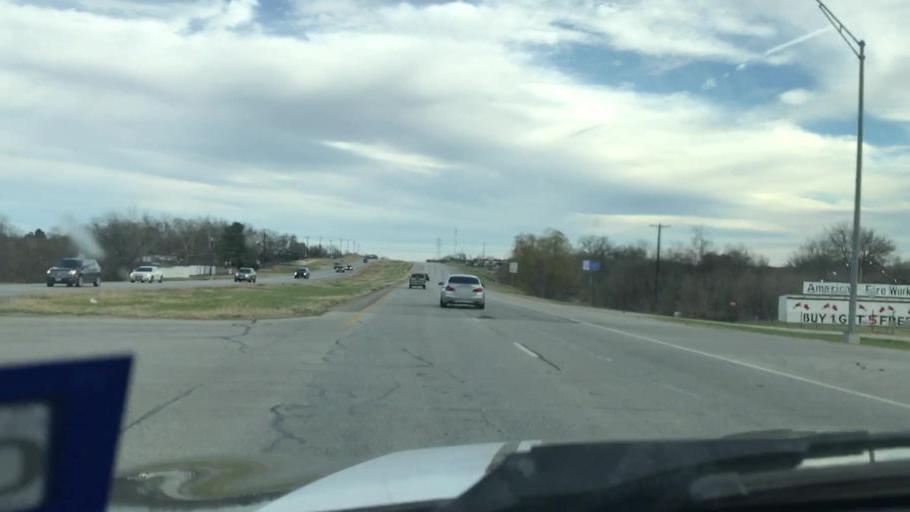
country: US
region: Texas
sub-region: Bastrop County
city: Elgin
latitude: 30.3345
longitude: -97.3604
